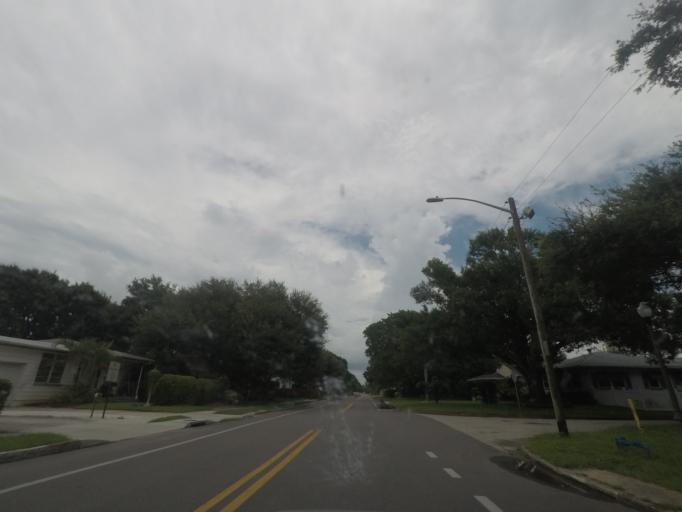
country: US
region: Florida
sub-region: Pinellas County
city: Lealman
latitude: 27.7993
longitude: -82.6504
